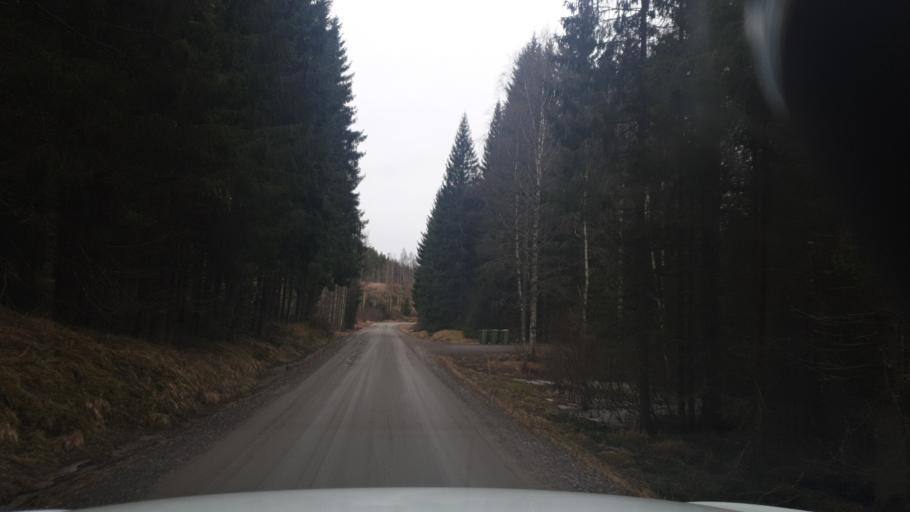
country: NO
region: Ostfold
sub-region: Romskog
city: Romskog
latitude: 59.7002
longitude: 11.9463
